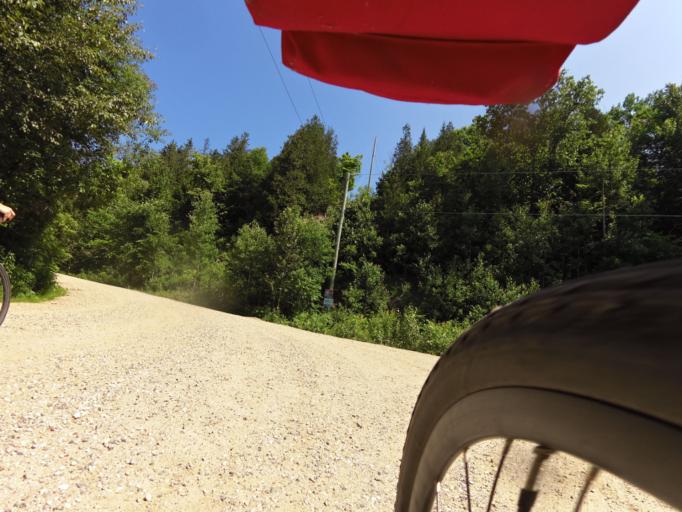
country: CA
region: Quebec
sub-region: Outaouais
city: Wakefield
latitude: 45.7765
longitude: -75.9434
